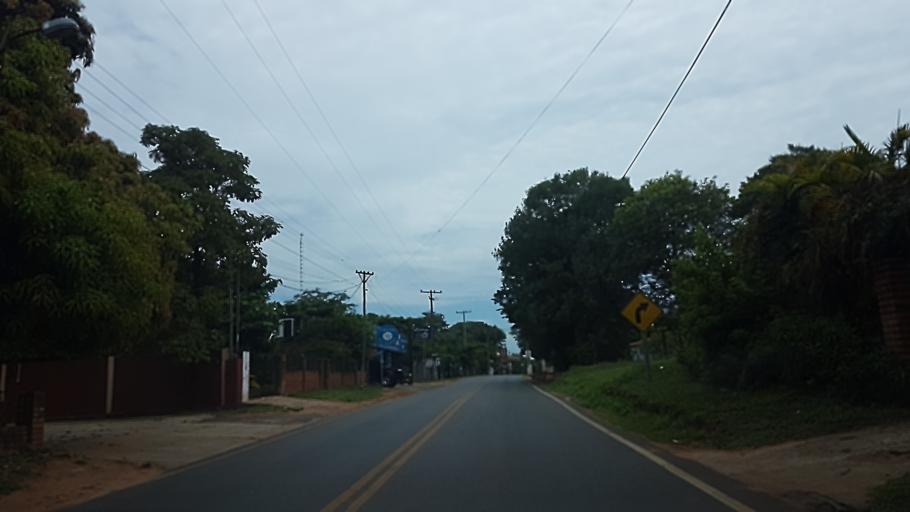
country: PY
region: Central
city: Capiata
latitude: -25.3318
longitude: -57.4602
